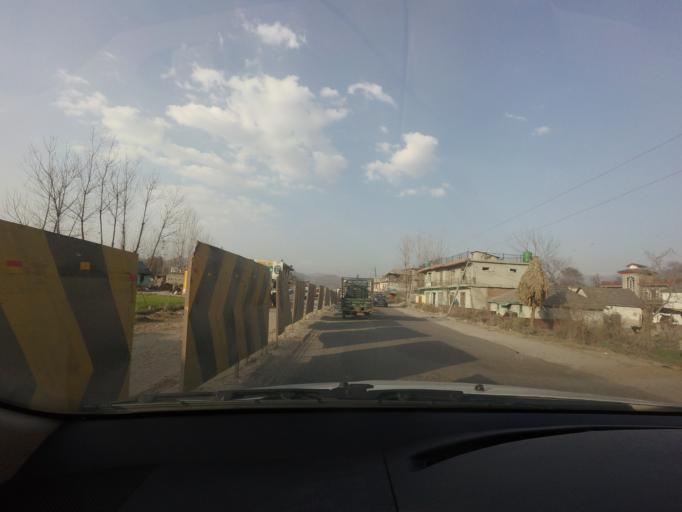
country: IN
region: Himachal Pradesh
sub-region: Mandi
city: Sundarnagar
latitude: 31.5939
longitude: 76.9241
